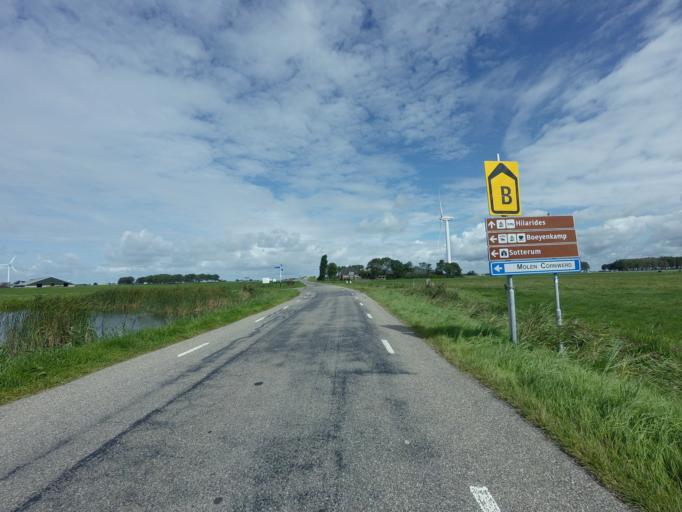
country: NL
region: Friesland
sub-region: Sudwest Fryslan
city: Makkum
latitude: 53.0889
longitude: 5.4210
